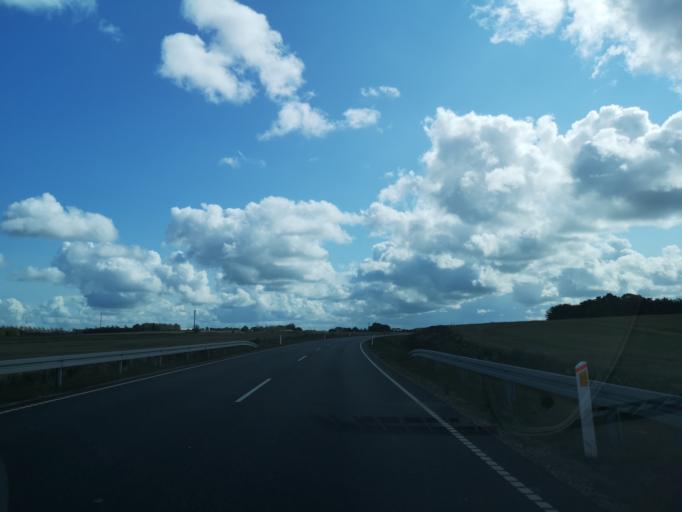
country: DK
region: Central Jutland
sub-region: Holstebro Kommune
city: Holstebro
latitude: 56.3952
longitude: 8.5753
